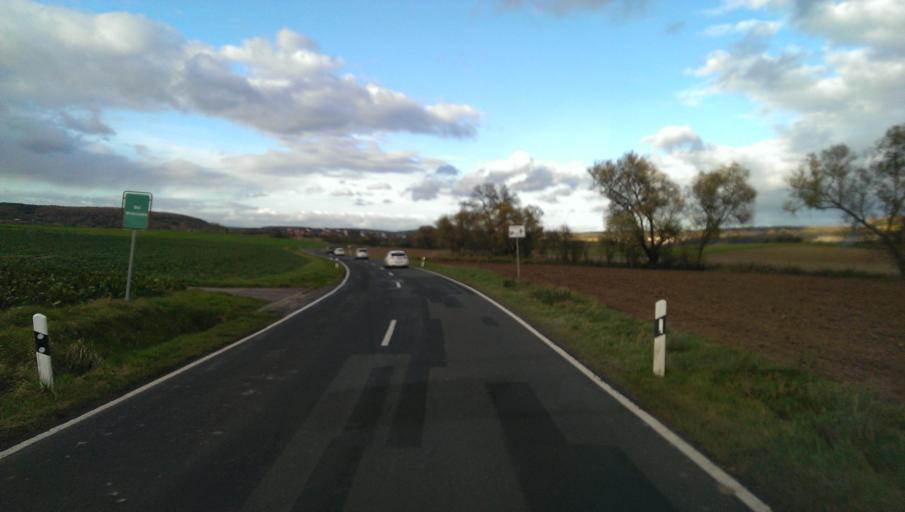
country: DE
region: Bavaria
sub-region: Regierungsbezirk Unterfranken
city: Zellingen
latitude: 49.8808
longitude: 9.8049
